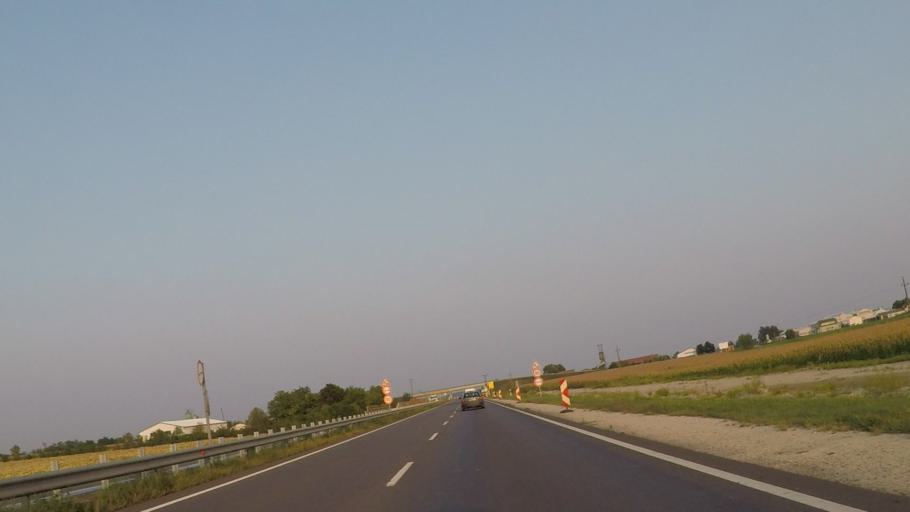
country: HU
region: Pest
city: Cegled
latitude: 47.1950
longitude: 19.8211
